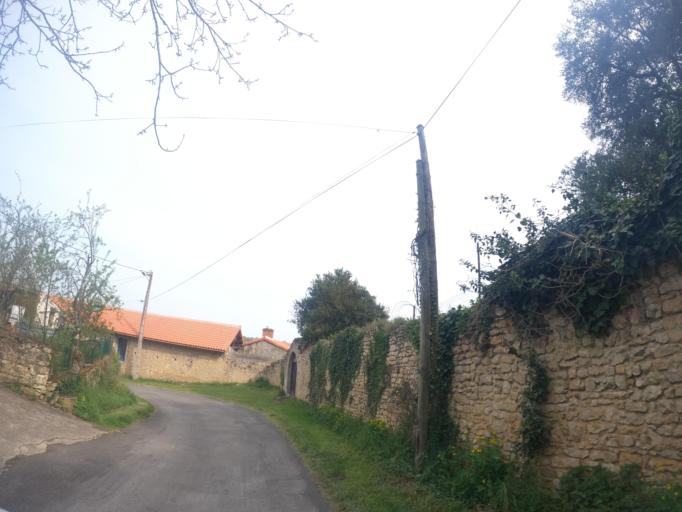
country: FR
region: Poitou-Charentes
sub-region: Departement des Deux-Sevres
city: Saint-Varent
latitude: 46.9142
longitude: -0.1913
